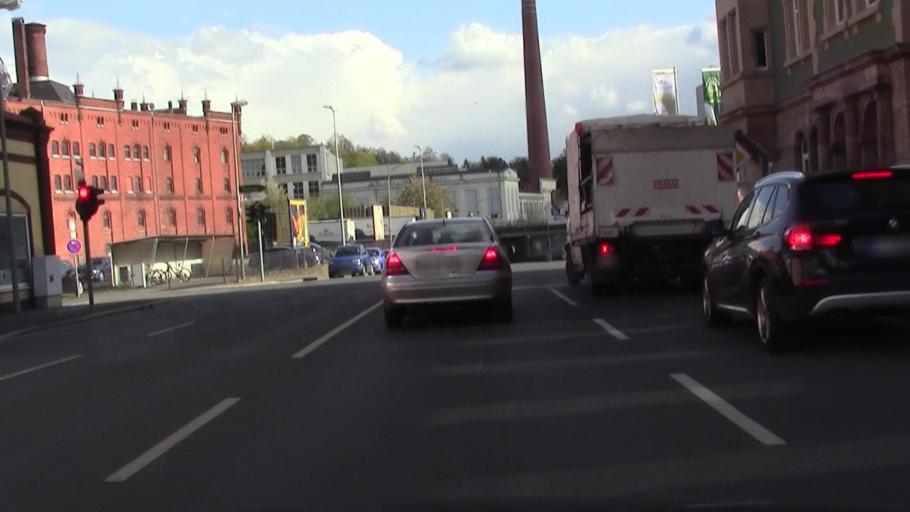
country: DE
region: Bavaria
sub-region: Upper Franconia
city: Kulmbach
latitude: 50.1109
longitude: 11.4483
